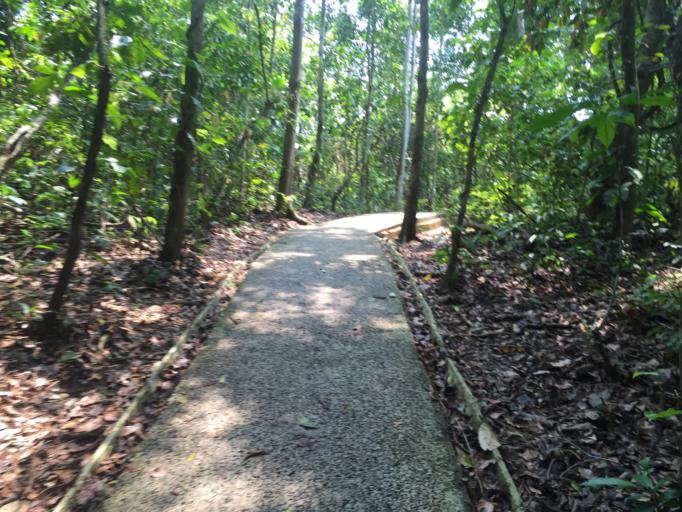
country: CR
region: Puntarenas
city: Quepos
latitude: 9.3842
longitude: -84.1428
